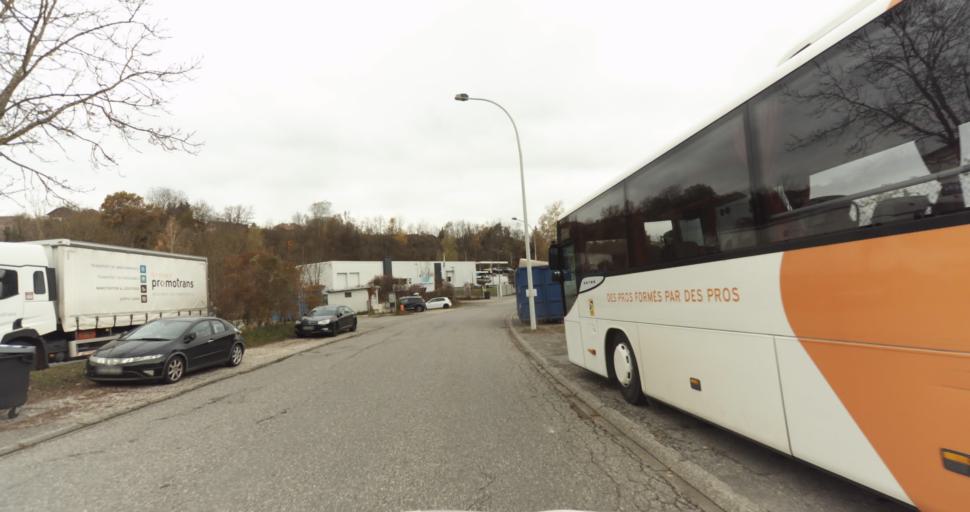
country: FR
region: Rhone-Alpes
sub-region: Departement de la Haute-Savoie
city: Annecy
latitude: 45.8825
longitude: 6.1134
